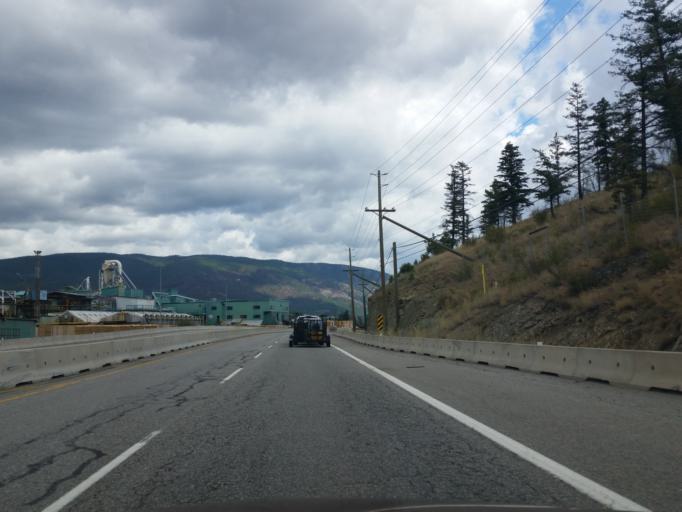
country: CA
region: British Columbia
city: West Kelowna
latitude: 49.8171
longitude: -119.6536
